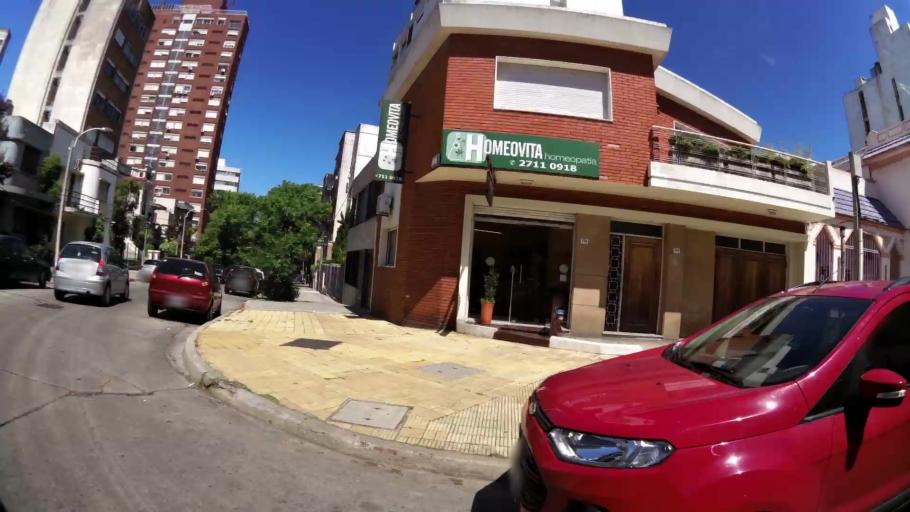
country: UY
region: Montevideo
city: Montevideo
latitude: -34.9166
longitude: -56.1562
